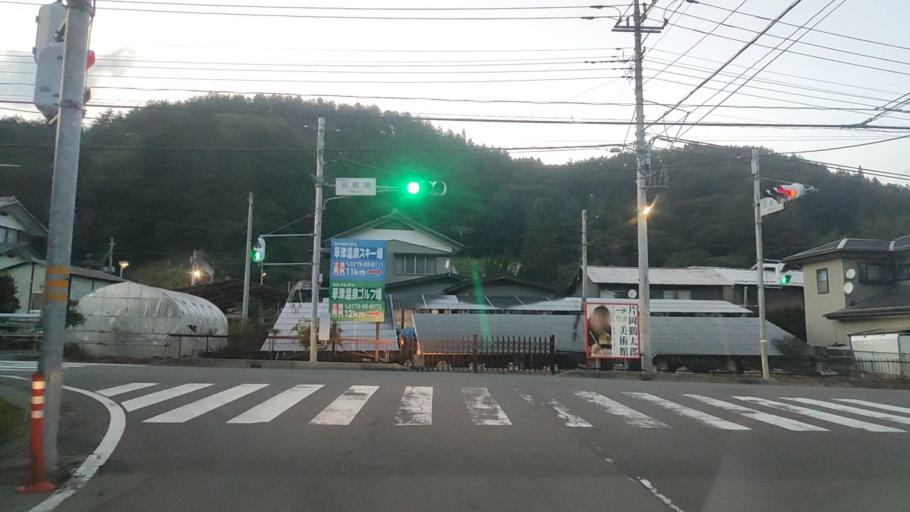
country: JP
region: Gunma
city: Nakanojomachi
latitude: 36.5492
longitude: 138.6056
